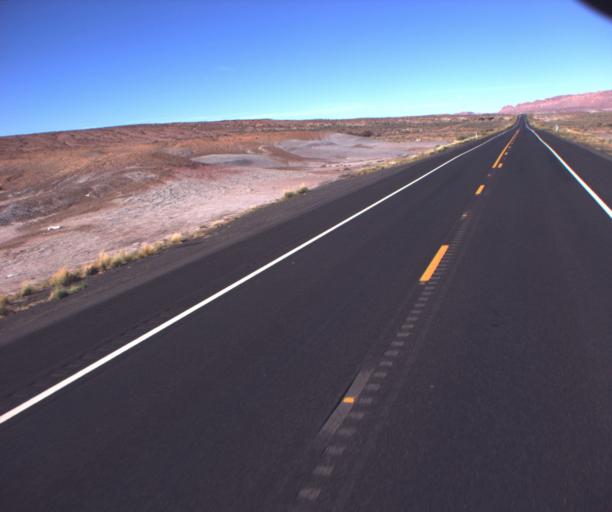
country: US
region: Arizona
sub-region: Coconino County
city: Tuba City
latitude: 36.1361
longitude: -111.3960
